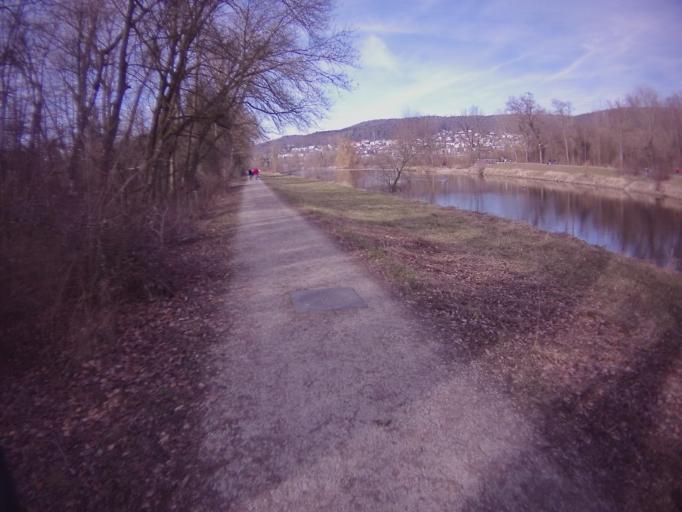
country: CH
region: Zurich
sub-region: Bezirk Dietikon
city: Geroldswil
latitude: 47.4127
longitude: 8.4078
